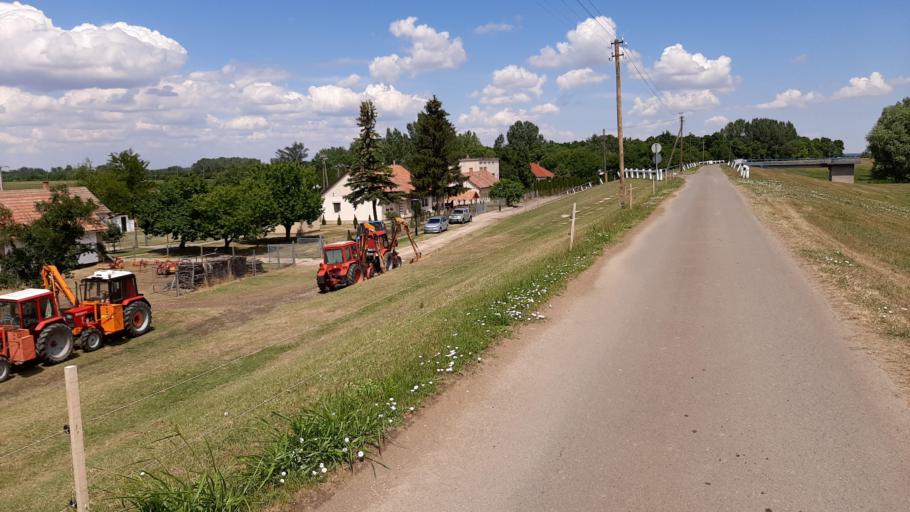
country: HU
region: Csongrad
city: Csanytelek
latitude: 46.6217
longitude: 20.1558
